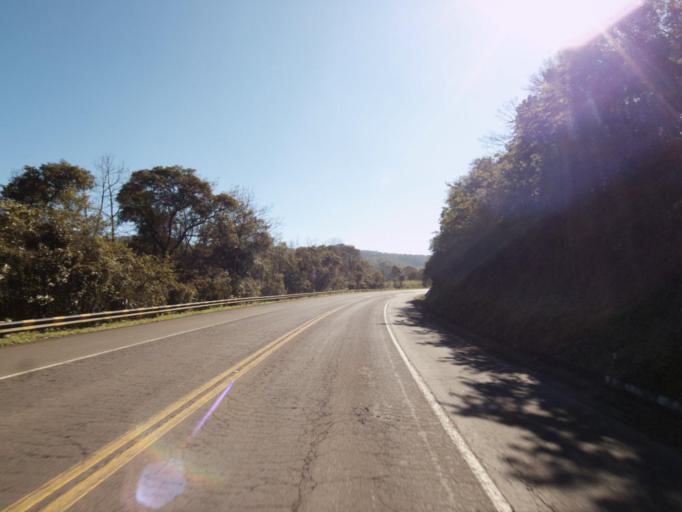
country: BR
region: Rio Grande do Sul
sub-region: Frederico Westphalen
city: Frederico Westphalen
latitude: -27.0314
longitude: -53.2353
